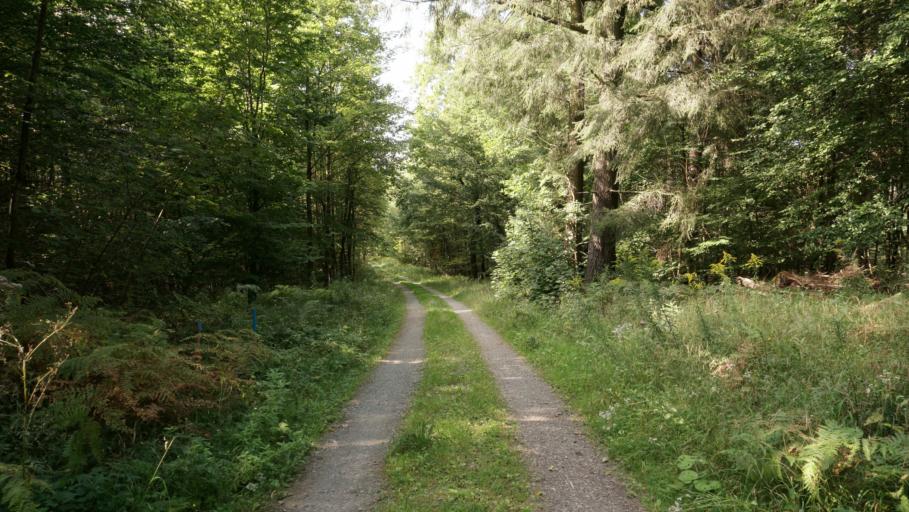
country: DE
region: Baden-Wuerttemberg
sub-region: Karlsruhe Region
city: Reichartshausen
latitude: 49.4050
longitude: 8.9607
